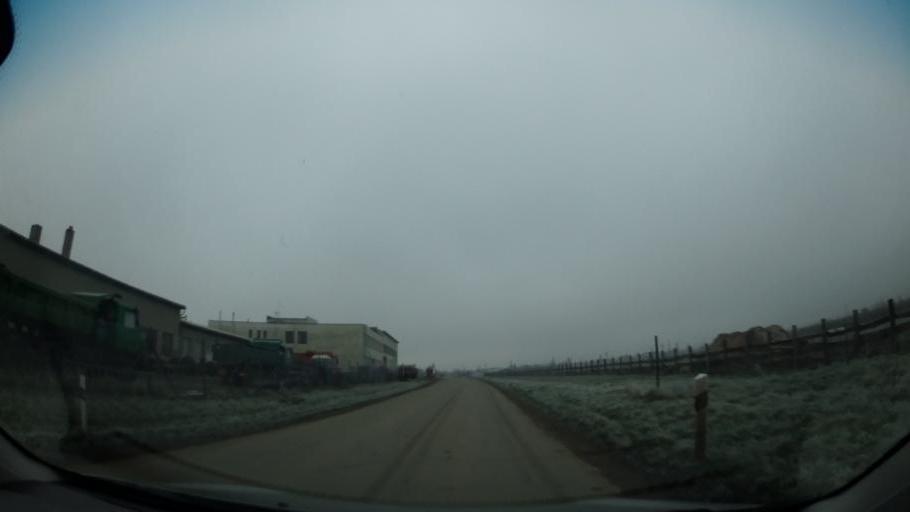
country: CZ
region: Vysocina
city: Mohelno
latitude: 49.1244
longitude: 16.1980
